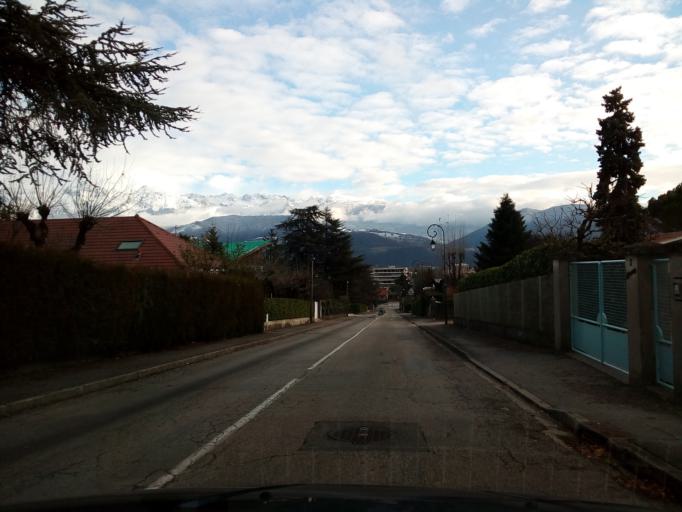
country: FR
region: Rhone-Alpes
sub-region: Departement de l'Isere
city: La Tronche
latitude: 45.2092
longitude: 5.7534
